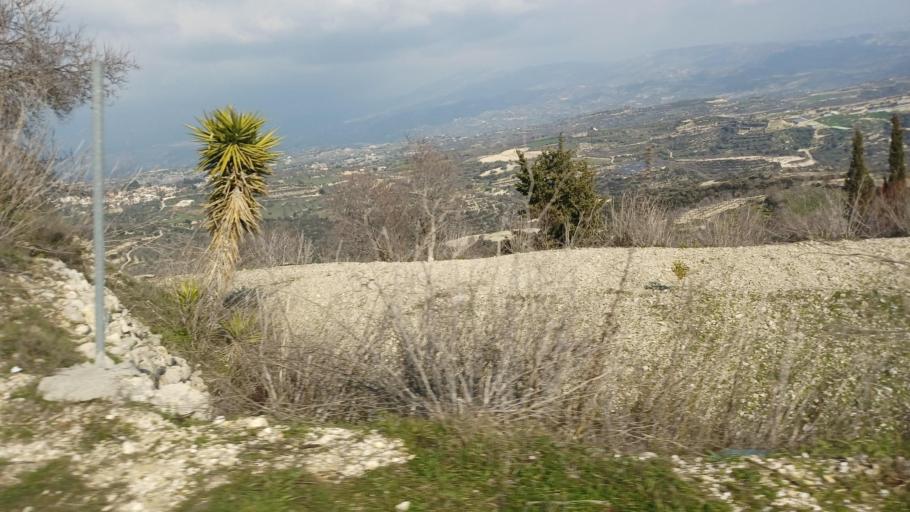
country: CY
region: Pafos
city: Mesogi
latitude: 34.8327
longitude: 32.4919
